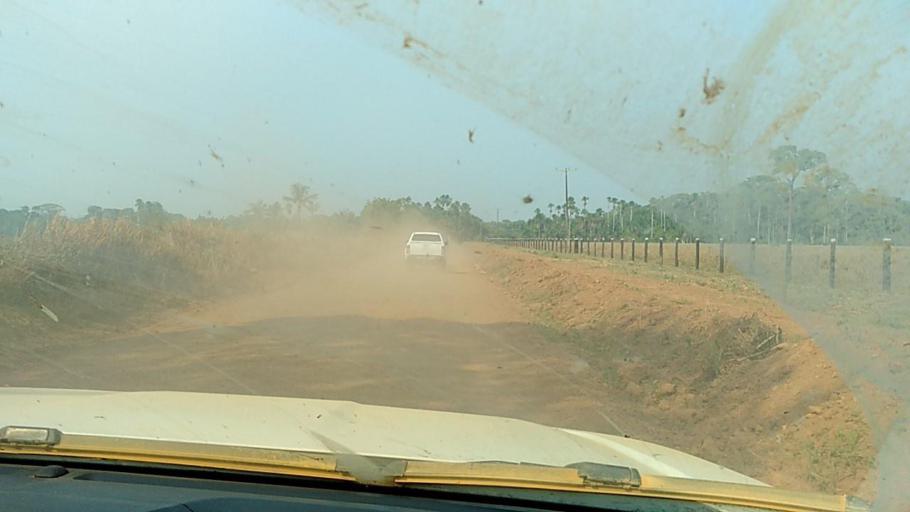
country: BR
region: Rondonia
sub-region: Porto Velho
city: Porto Velho
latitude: -8.7853
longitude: -64.0911
